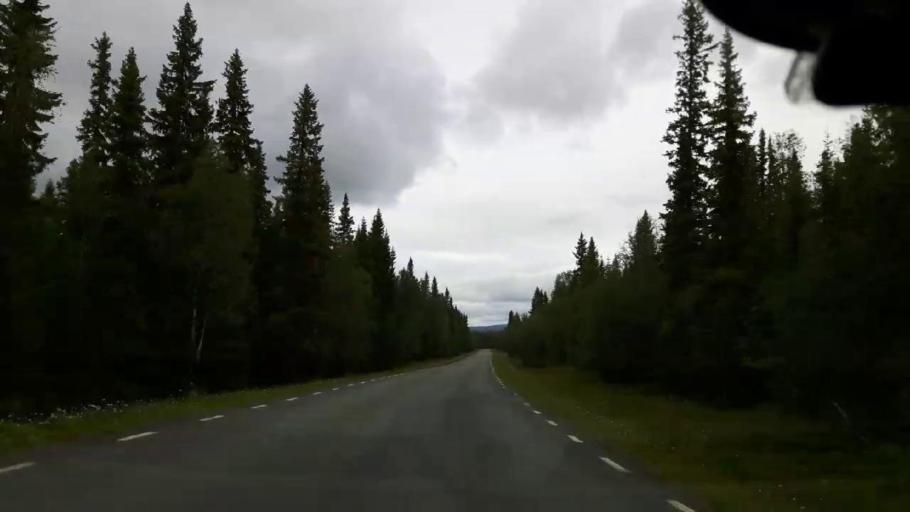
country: SE
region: Jaemtland
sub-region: Krokoms Kommun
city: Valla
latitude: 63.6117
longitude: 13.8117
